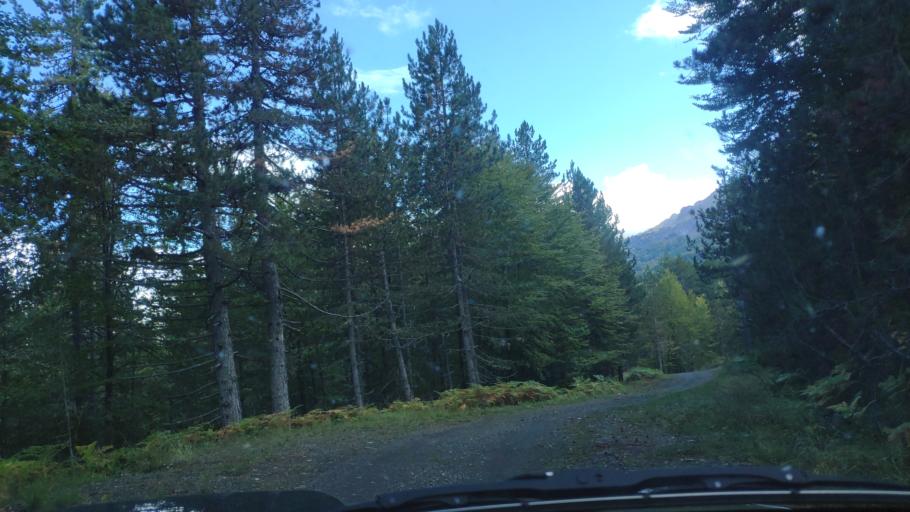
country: AL
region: Korce
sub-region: Rrethi i Devollit
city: Miras
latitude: 40.3452
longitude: 20.8996
